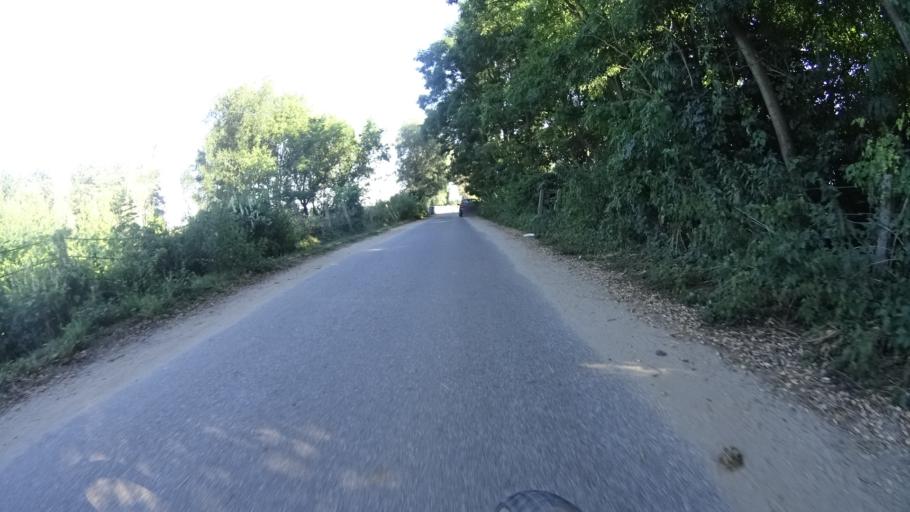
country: PL
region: Masovian Voivodeship
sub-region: Powiat bialobrzeski
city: Wysmierzyce
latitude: 51.6624
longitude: 20.8649
